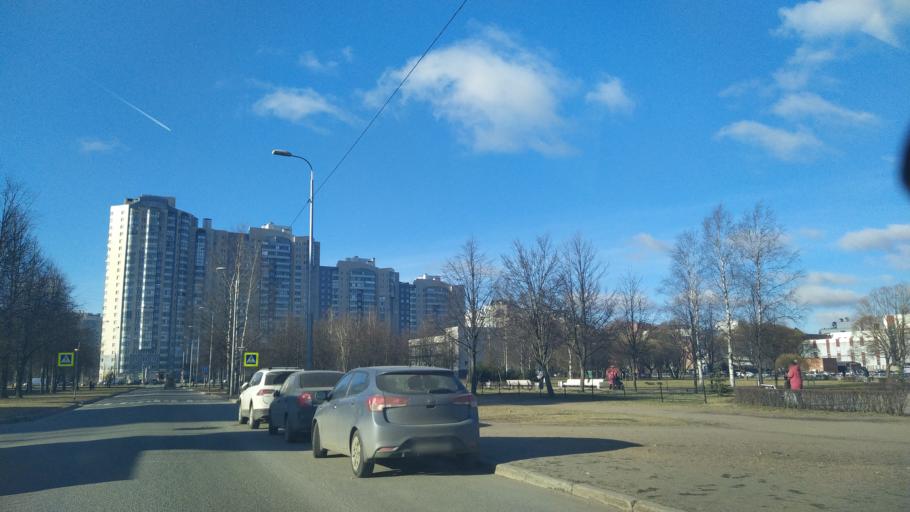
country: RU
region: Leningrad
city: Akademicheskoe
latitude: 60.0088
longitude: 30.3984
